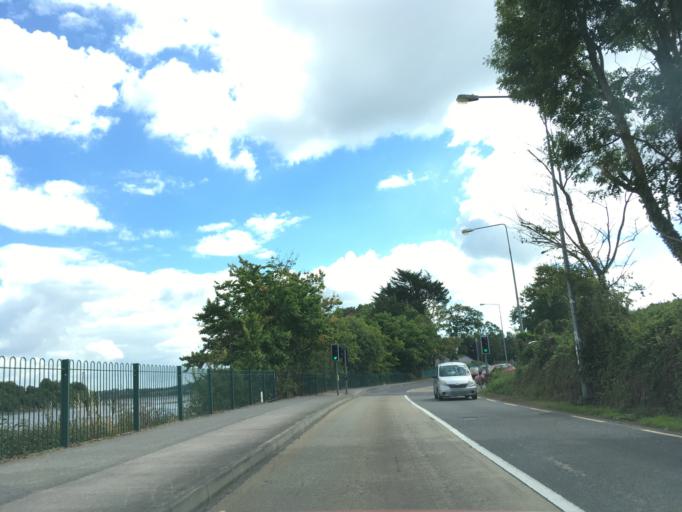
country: IE
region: Munster
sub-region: County Cork
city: Carrigaline
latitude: 51.8121
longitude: -8.3801
